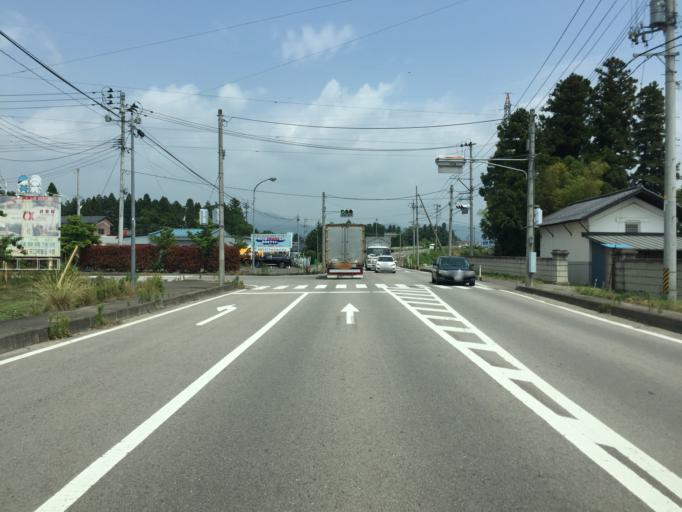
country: JP
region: Fukushima
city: Fukushima-shi
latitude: 37.7532
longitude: 140.4016
